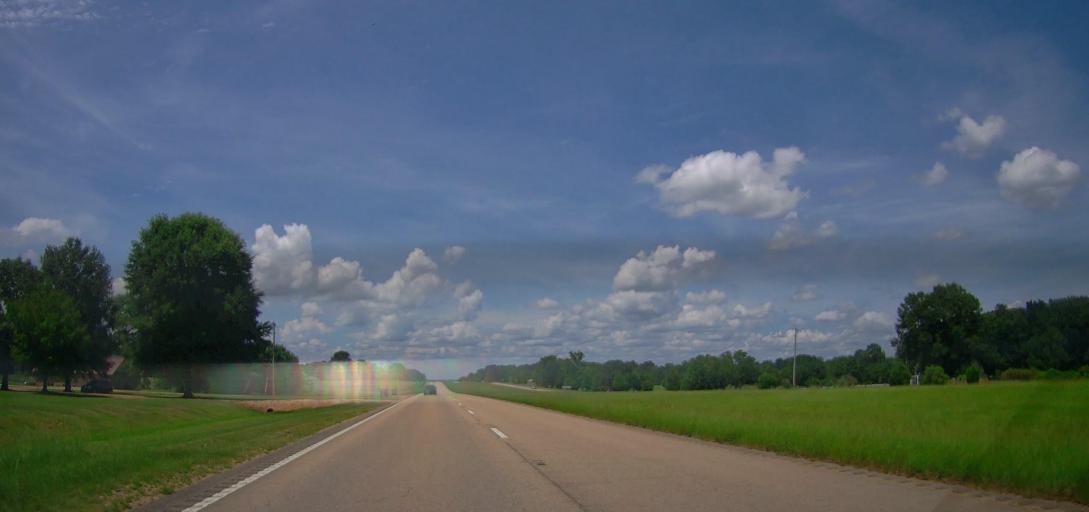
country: US
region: Mississippi
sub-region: Lee County
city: Nettleton
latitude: 34.0197
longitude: -88.6325
